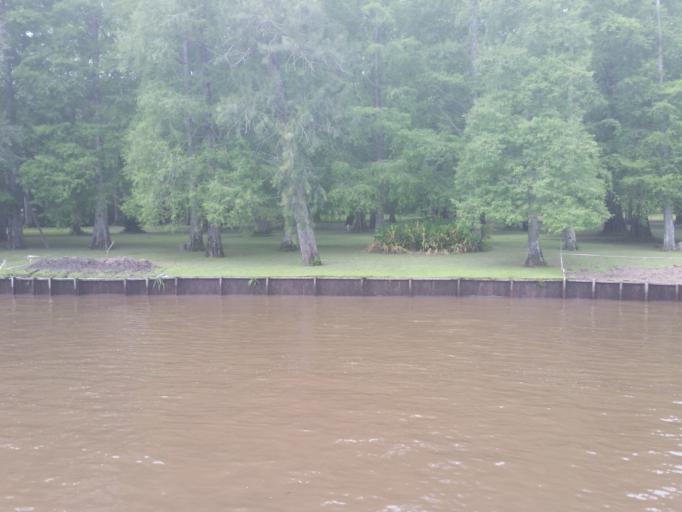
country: AR
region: Buenos Aires
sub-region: Partido de Tigre
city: Tigre
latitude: -34.3943
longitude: -58.5725
